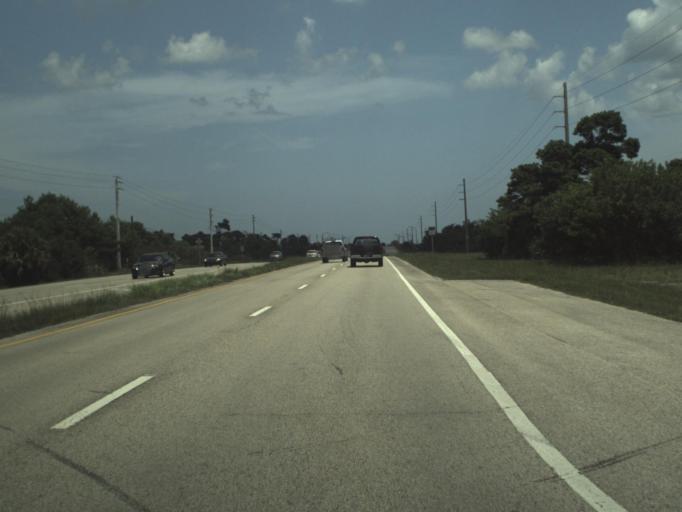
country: US
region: Florida
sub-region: Martin County
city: Hobe Sound
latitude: 27.0493
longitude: -80.1259
